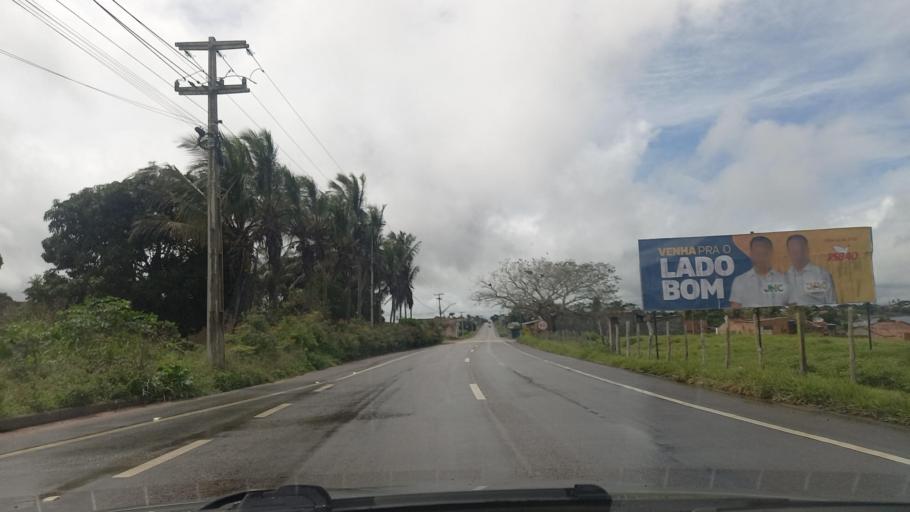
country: BR
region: Alagoas
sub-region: Limoeiro De Anadia
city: Limoeiro de Anadia
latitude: -9.7592
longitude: -36.5668
